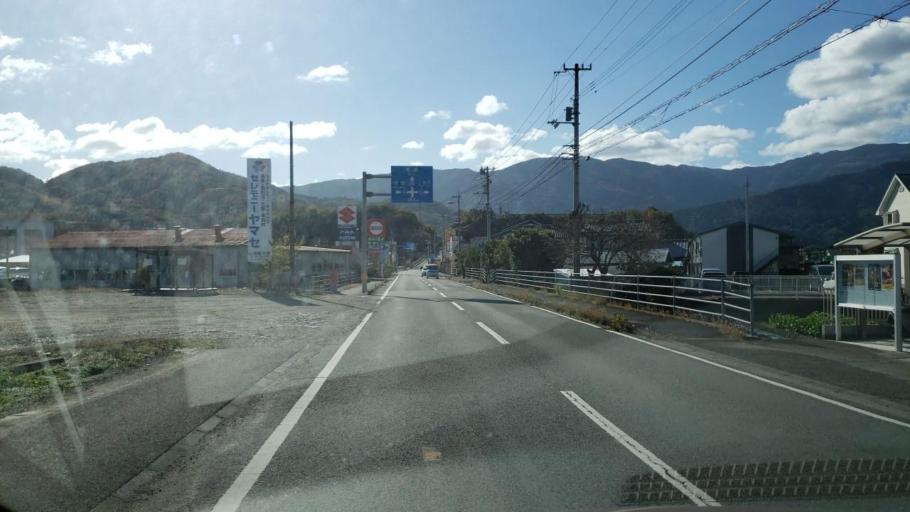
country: JP
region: Tokushima
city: Wakimachi
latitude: 34.0599
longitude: 134.2381
